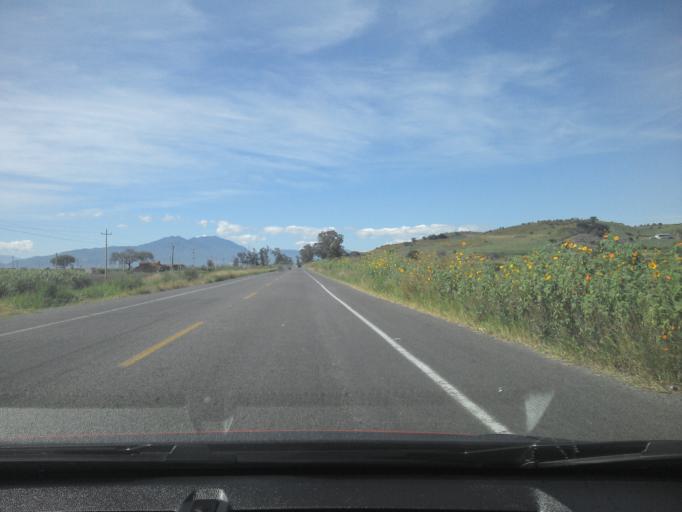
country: MX
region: Jalisco
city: El Refugio
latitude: 20.6659
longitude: -103.7655
